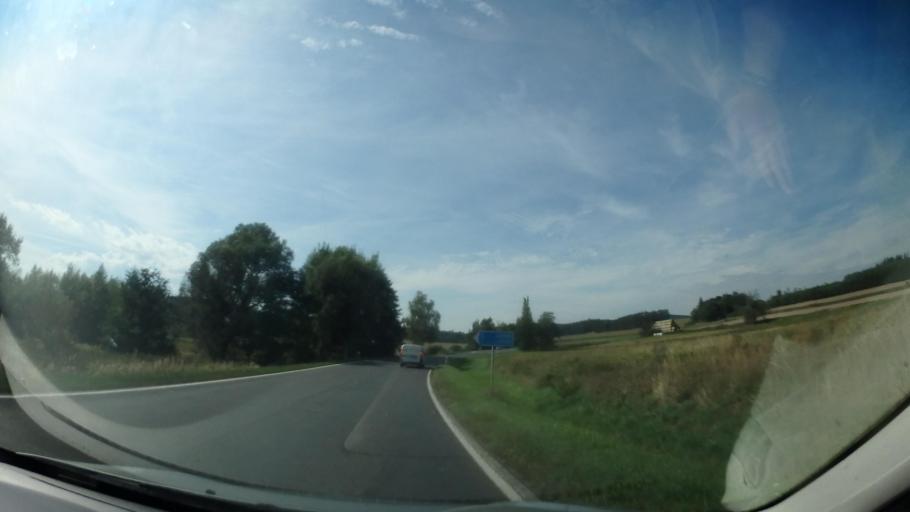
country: CZ
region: Jihocesky
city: Radomysl
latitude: 49.2947
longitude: 14.0293
